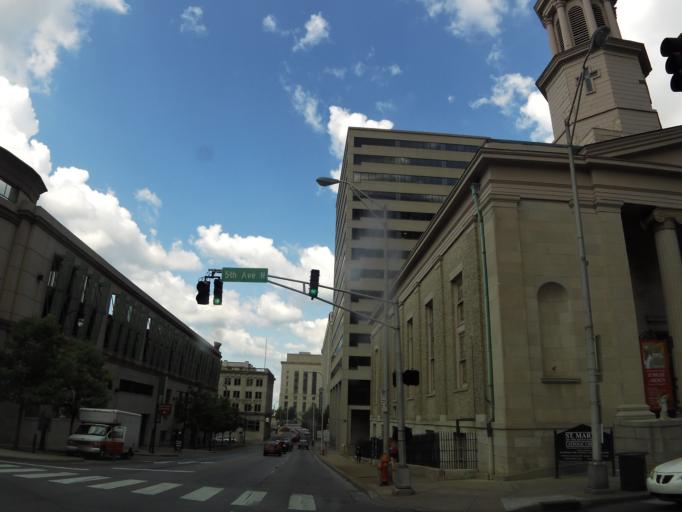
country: US
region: Tennessee
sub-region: Davidson County
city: Nashville
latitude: 36.1658
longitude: -86.7820
